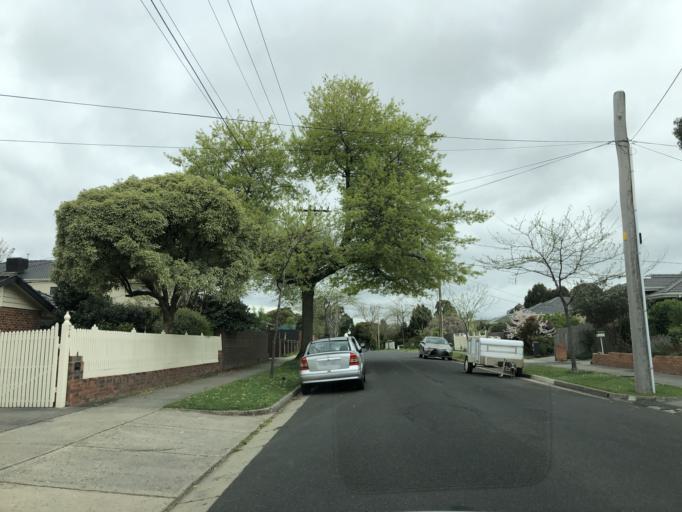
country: AU
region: Victoria
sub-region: Whitehorse
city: Forest Hill
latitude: -37.8391
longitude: 145.1667
